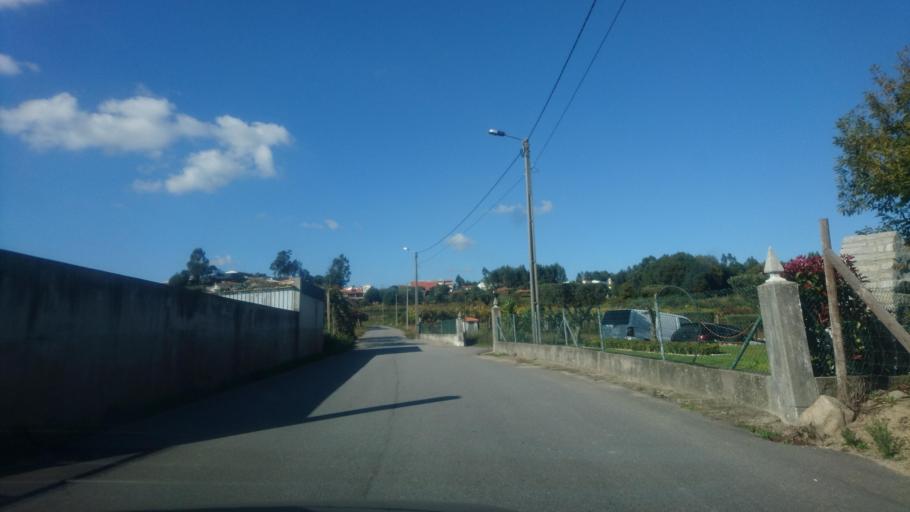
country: PT
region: Porto
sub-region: Paredes
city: Madalena
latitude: 41.2250
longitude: -8.3405
